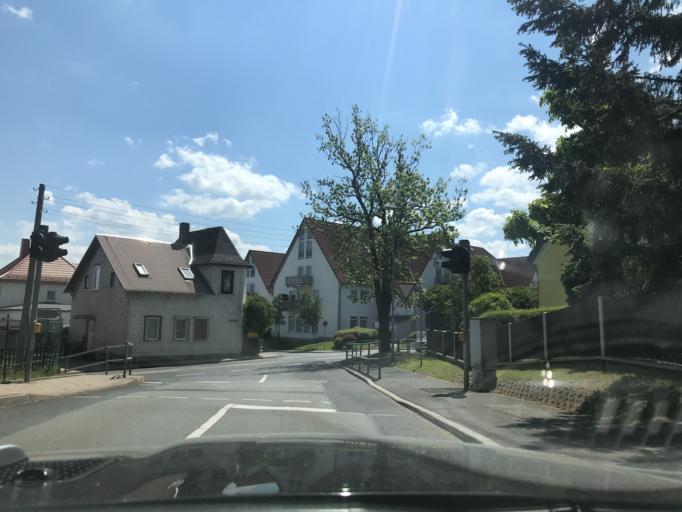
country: DE
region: Thuringia
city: Neuhaus
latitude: 50.7004
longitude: 10.9278
